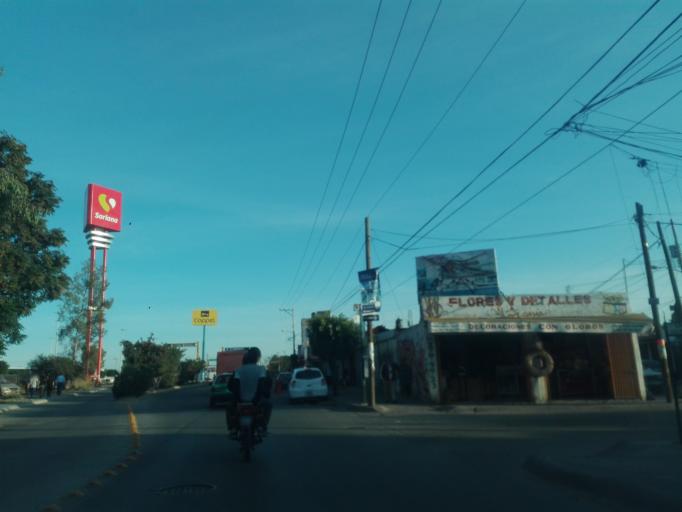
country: MX
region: Guanajuato
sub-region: Leon
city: San Jose de Duran (Los Troncoso)
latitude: 21.0834
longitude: -101.6428
